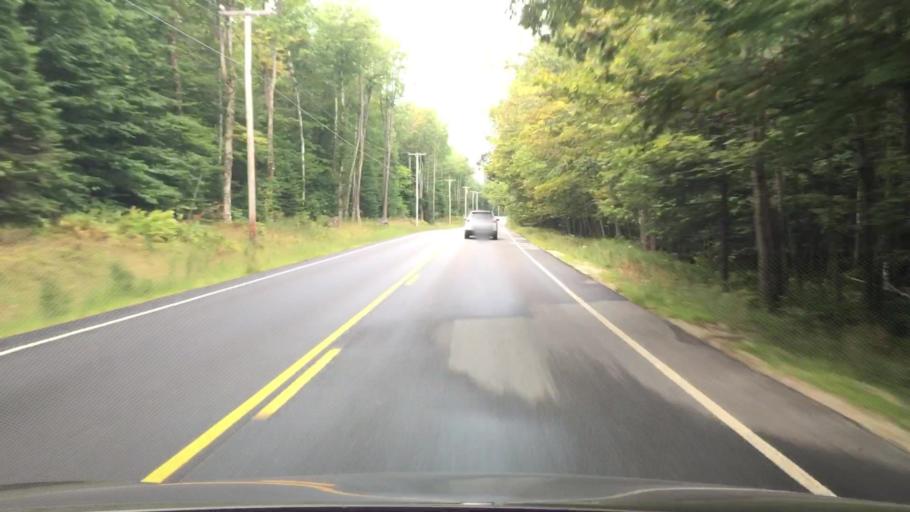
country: US
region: Maine
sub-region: Oxford County
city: Hartford
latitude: 44.3652
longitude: -70.3254
